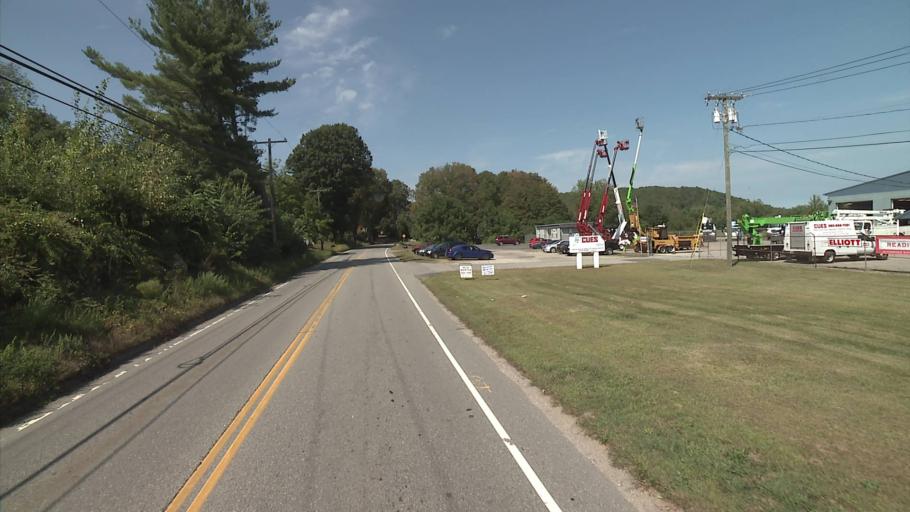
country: US
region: Connecticut
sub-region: New London County
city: Baltic
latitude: 41.5754
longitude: -72.1378
